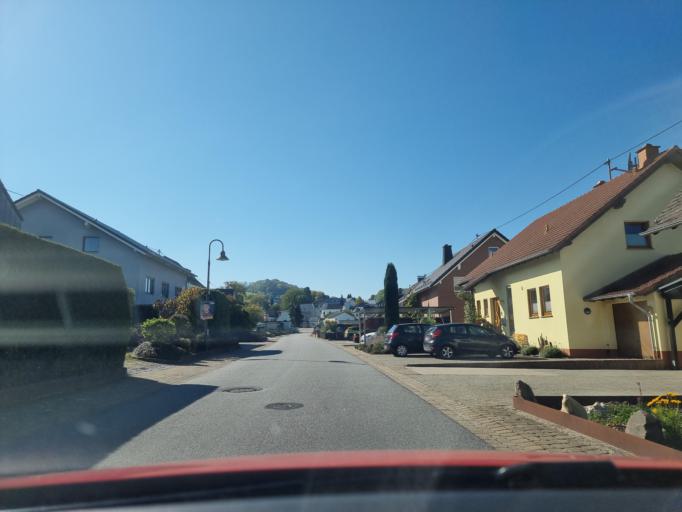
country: DE
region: Rheinland-Pfalz
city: Trierweiler
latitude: 49.7509
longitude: 6.5533
